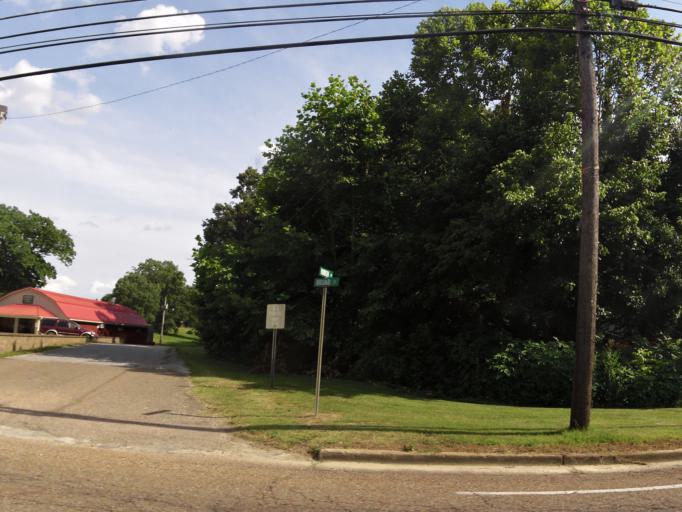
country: US
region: Tennessee
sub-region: Carroll County
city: Bruceton
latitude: 36.0338
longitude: -88.2710
